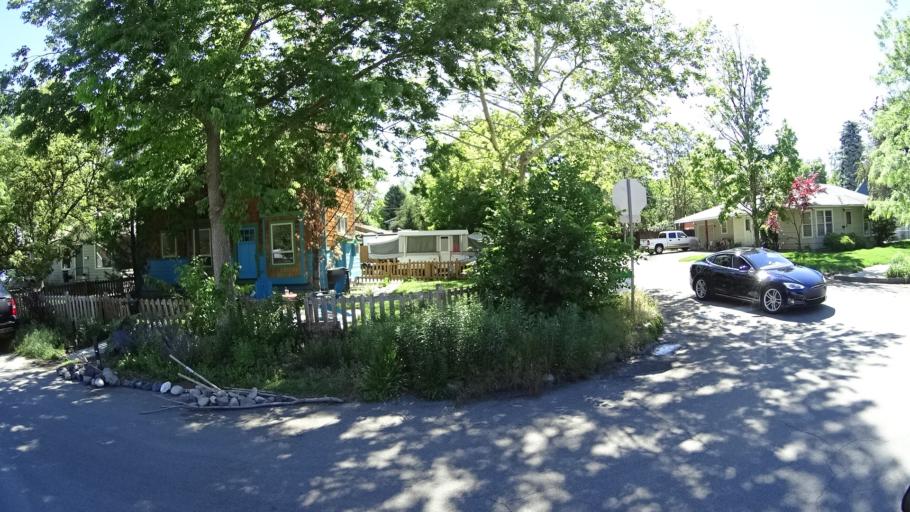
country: US
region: Idaho
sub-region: Ada County
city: Boise
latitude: 43.6392
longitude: -116.2134
